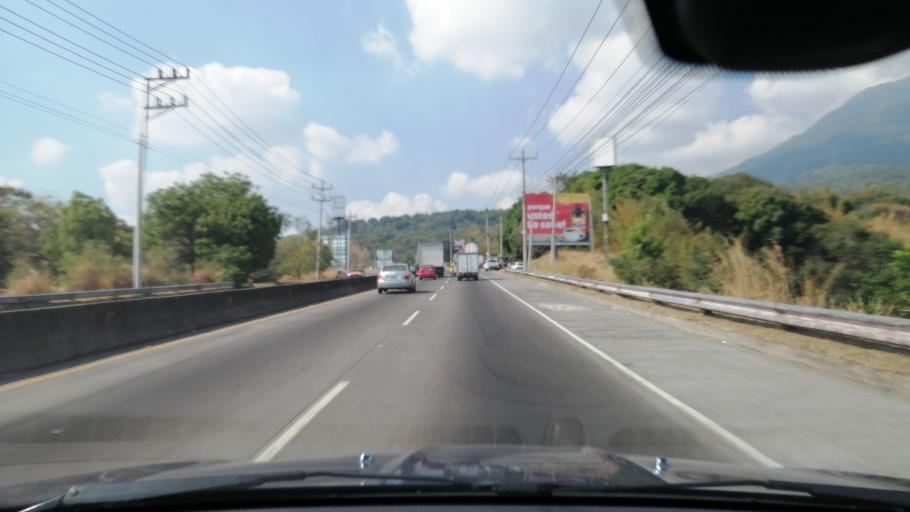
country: SV
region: San Salvador
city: Ayutuxtepeque
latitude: 13.7592
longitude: -89.2149
